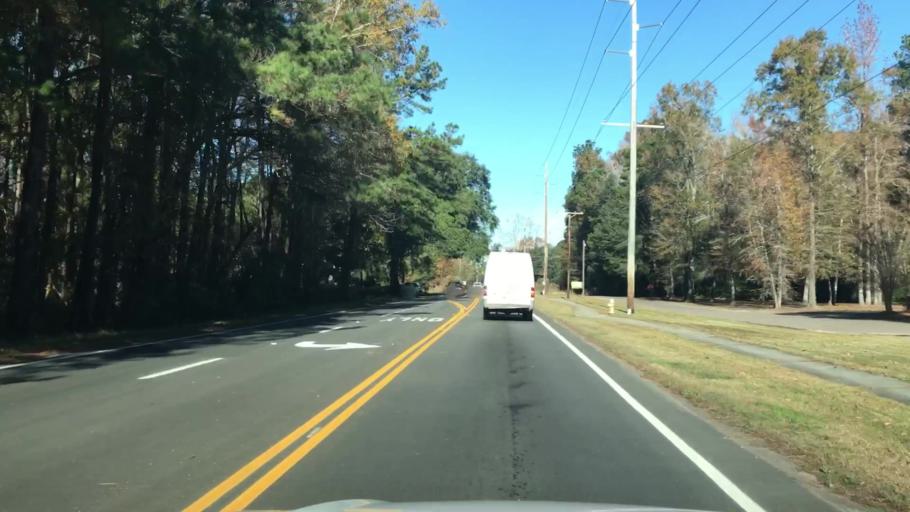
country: US
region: South Carolina
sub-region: Dorchester County
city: Summerville
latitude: 33.0022
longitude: -80.2324
